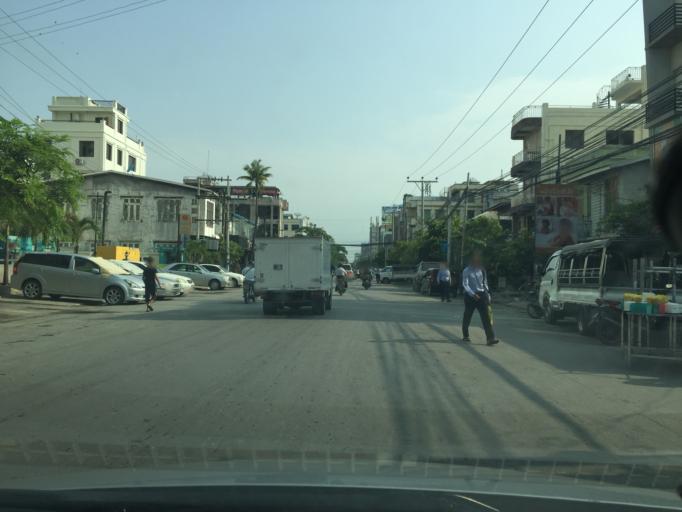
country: MM
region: Mandalay
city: Mandalay
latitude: 21.9733
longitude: 96.0822
